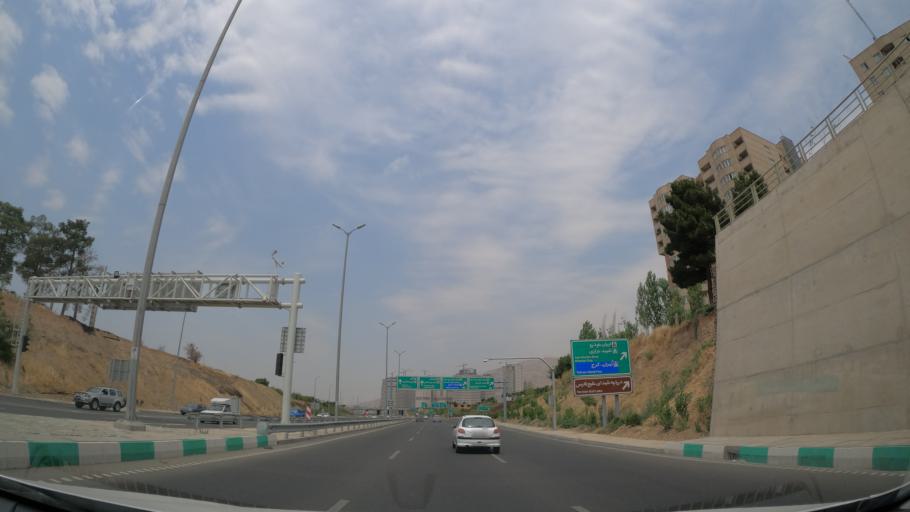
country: IR
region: Tehran
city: Shahr-e Qods
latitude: 35.7446
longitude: 51.1959
